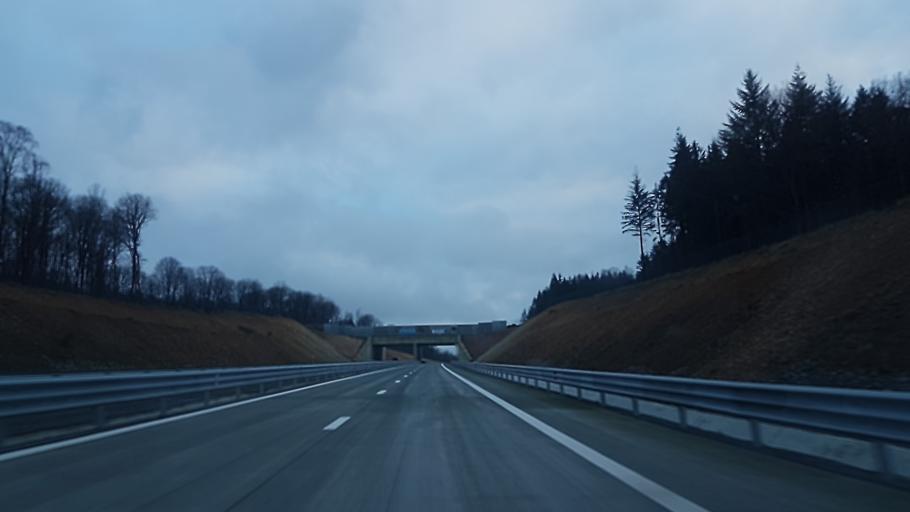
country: BE
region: Wallonia
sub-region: Province de Namur
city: Couvin
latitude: 50.0037
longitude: 4.5397
